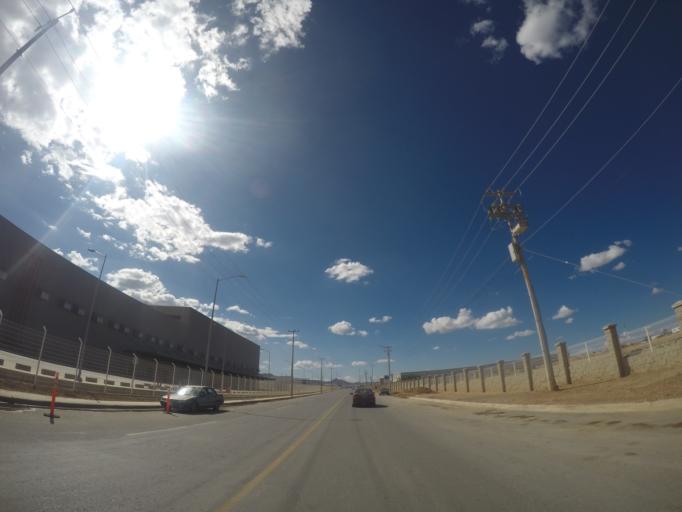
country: MX
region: San Luis Potosi
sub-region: Zaragoza
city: Cerro Gordo
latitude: 21.9753
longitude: -100.8541
